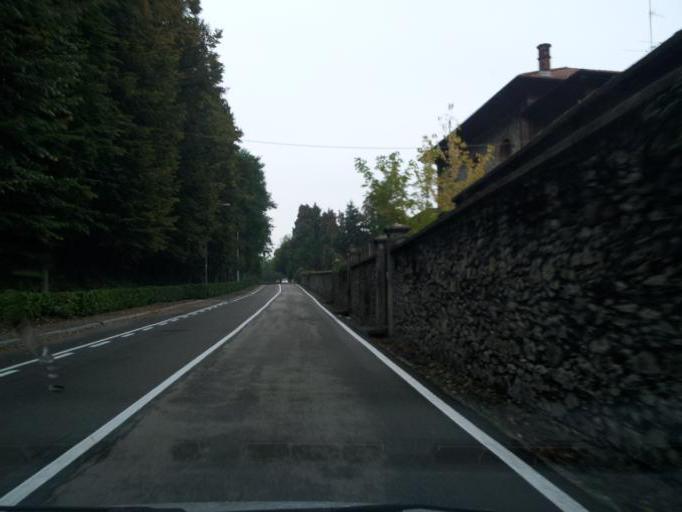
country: IT
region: Lombardy
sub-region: Provincia di Varese
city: Varano Borghi
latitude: 45.7694
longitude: 8.7048
